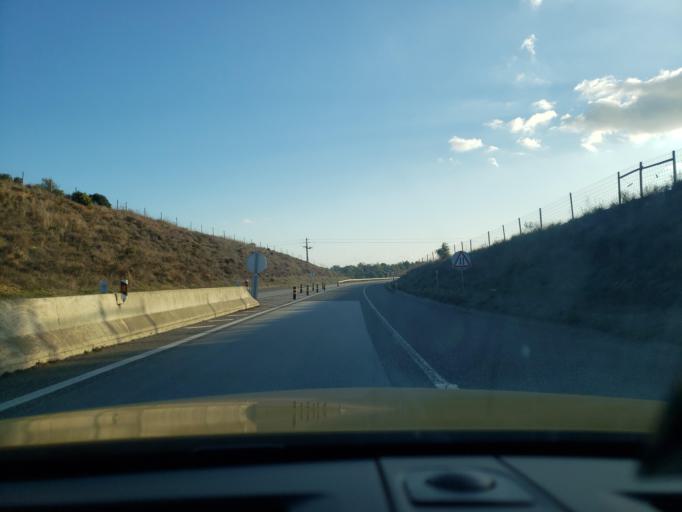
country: PT
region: Faro
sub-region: Portimao
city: Portimao
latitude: 37.1728
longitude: -8.5672
